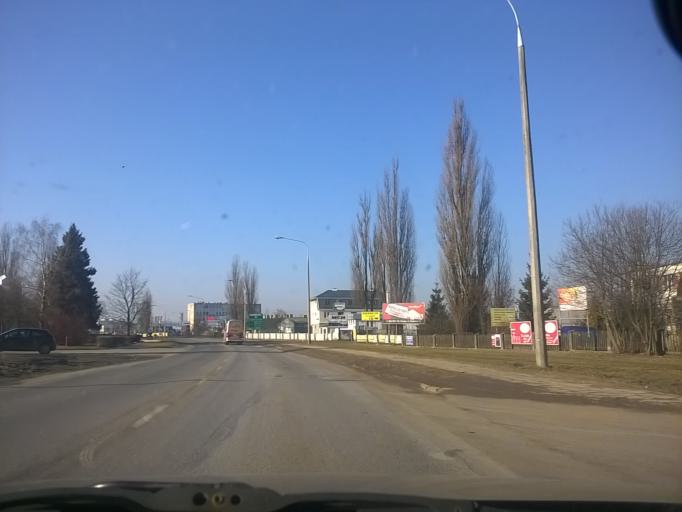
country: PL
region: Warmian-Masurian Voivodeship
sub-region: Powiat olsztynski
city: Olsztyn
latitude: 53.7851
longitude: 20.5380
